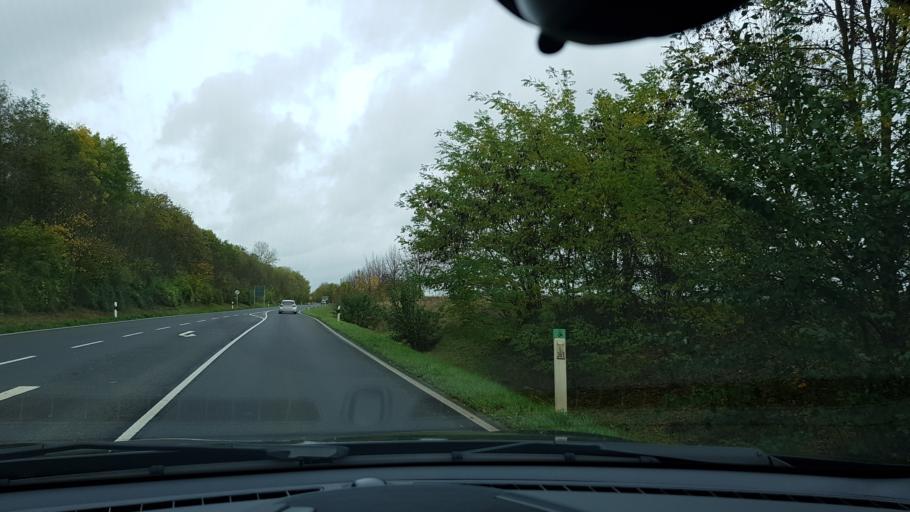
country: DE
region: North Rhine-Westphalia
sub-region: Regierungsbezirk Koln
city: Bedburg
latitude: 50.9998
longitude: 6.5852
